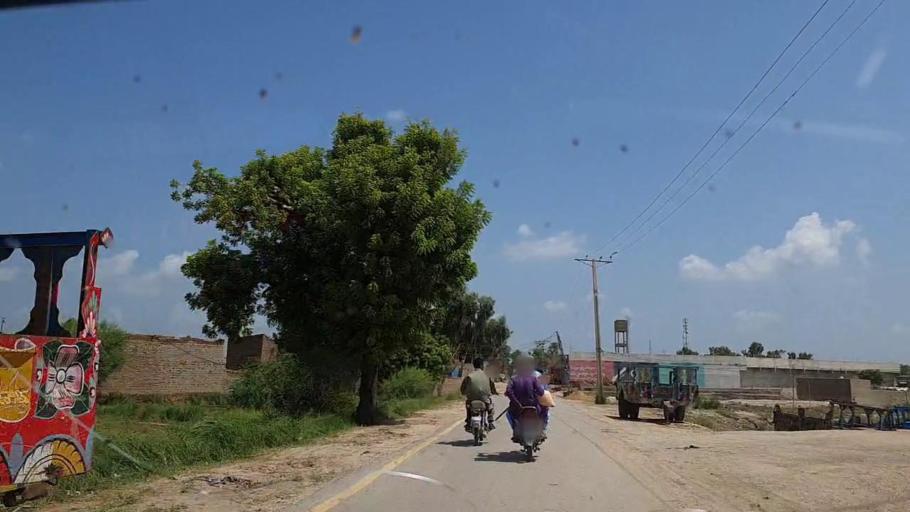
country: PK
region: Sindh
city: Tharu Shah
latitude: 26.9470
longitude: 68.1116
